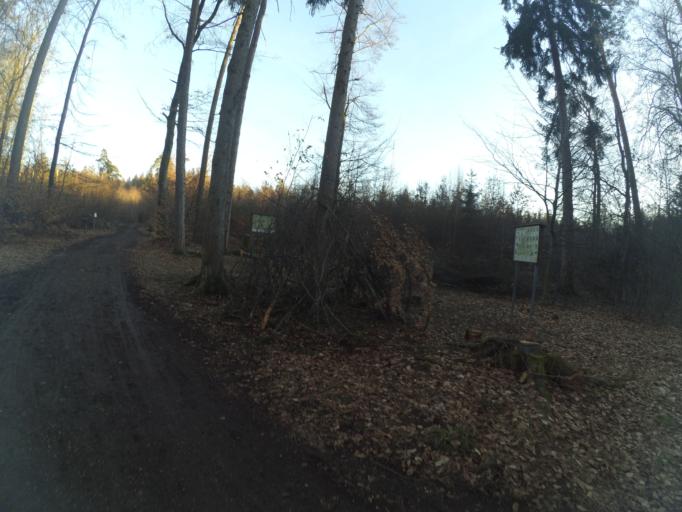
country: DE
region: Bavaria
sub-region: Swabia
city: Guenzburg
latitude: 48.4469
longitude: 10.3048
